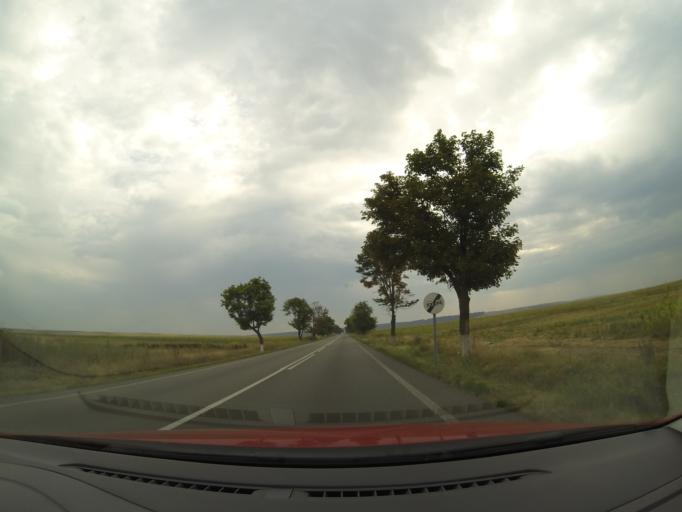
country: RO
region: Olt
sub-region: Comuna Bobicesti
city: Bobicesti
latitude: 44.3544
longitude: 24.1604
